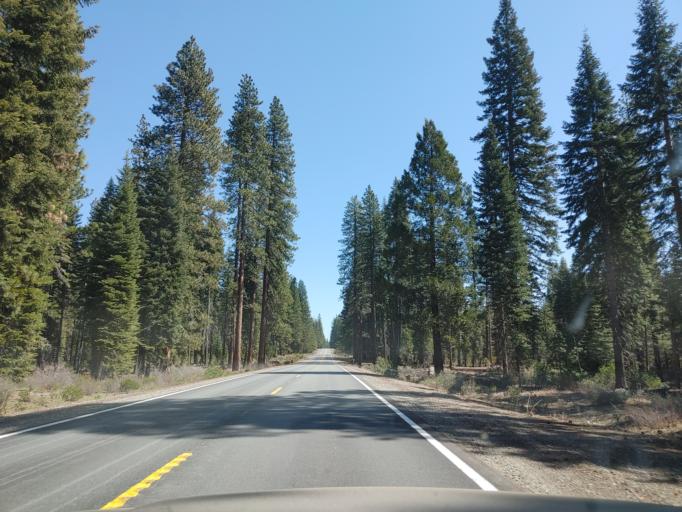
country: US
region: California
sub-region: Siskiyou County
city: McCloud
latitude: 41.2655
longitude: -121.9298
